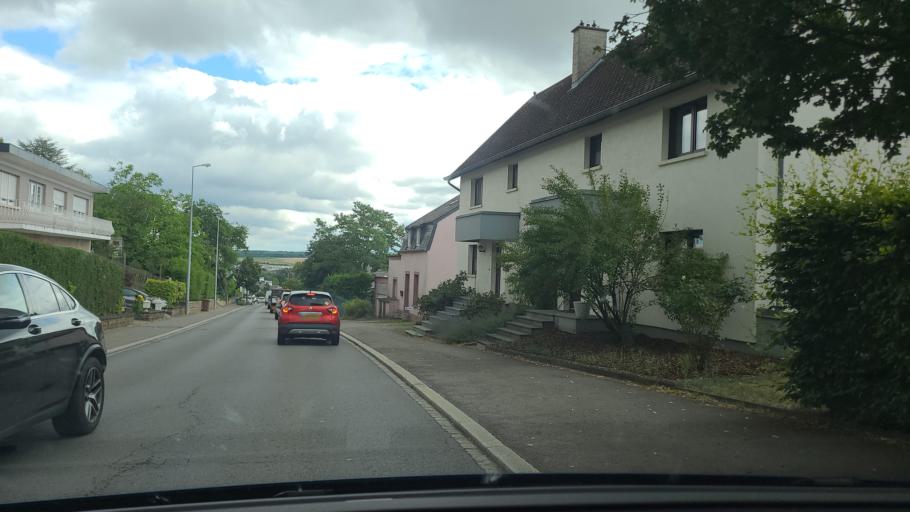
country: LU
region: Luxembourg
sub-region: Canton de Luxembourg
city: Hesperange
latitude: 49.5713
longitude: 6.1471
